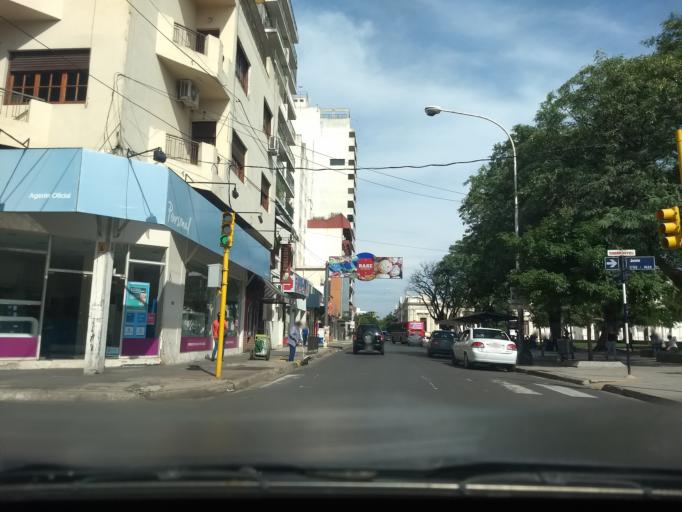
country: AR
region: Corrientes
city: Corrientes
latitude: -27.4682
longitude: -58.8304
